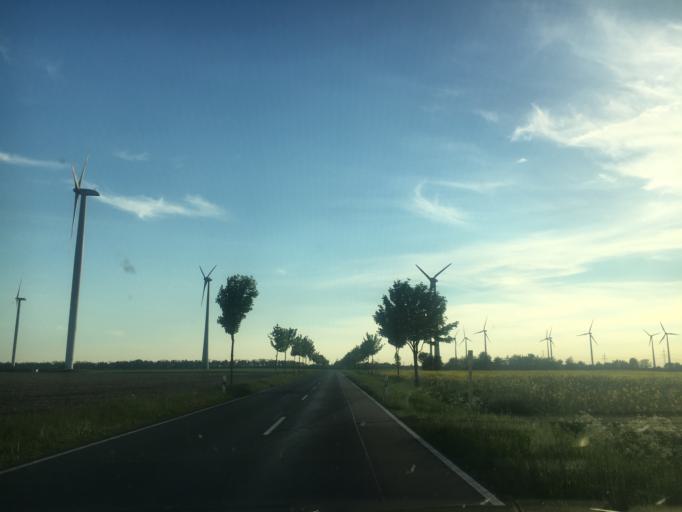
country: DE
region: Saxony-Anhalt
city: Raguhn
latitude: 51.7030
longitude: 12.2470
